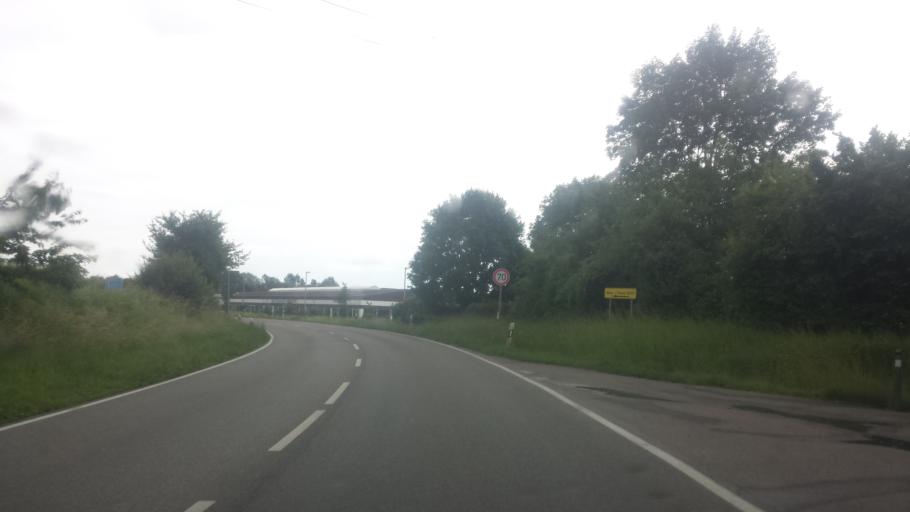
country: DE
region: Rheinland-Pfalz
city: Edenkoben
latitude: 49.2878
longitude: 8.1470
